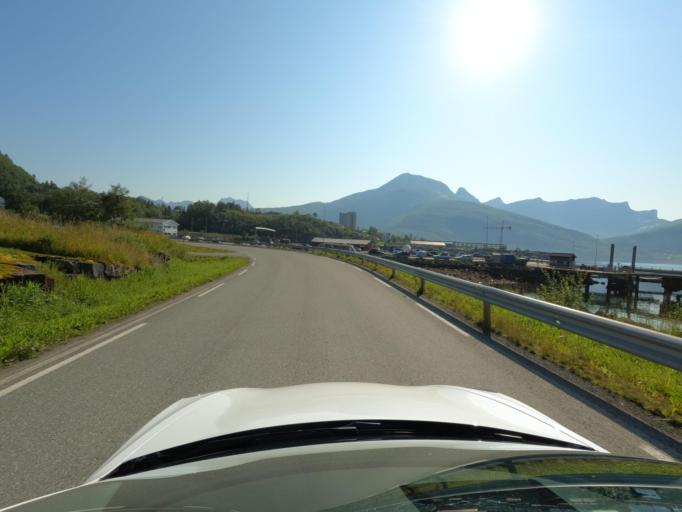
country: NO
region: Nordland
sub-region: Tysfjord
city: Kjopsvik
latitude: 68.0937
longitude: 16.3561
